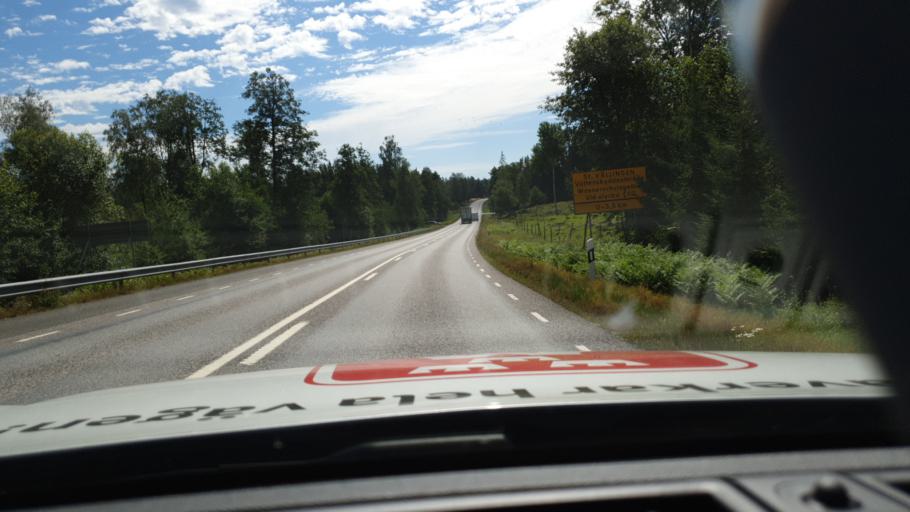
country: SE
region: Kronoberg
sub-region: Vaxjo Kommun
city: Lammhult
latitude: 57.1963
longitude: 14.5304
